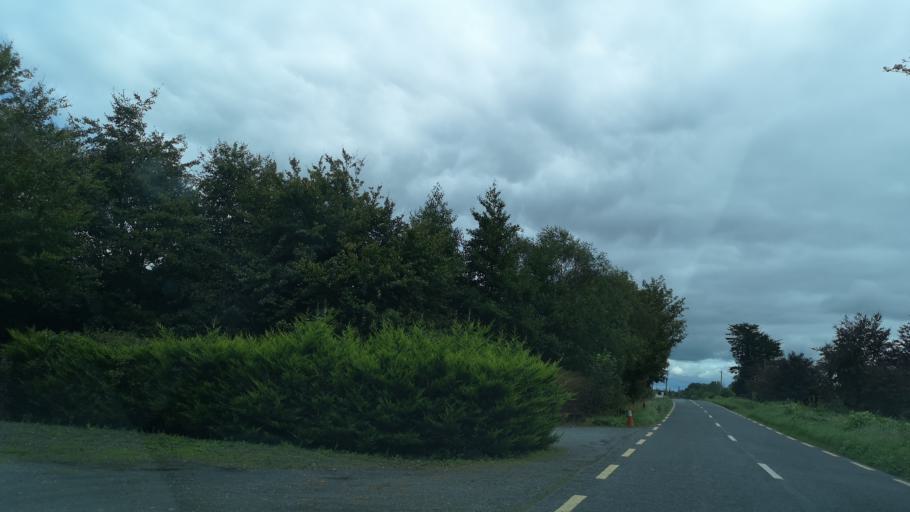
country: IE
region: Connaught
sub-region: County Galway
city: Ballinasloe
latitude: 53.3095
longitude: -8.1542
